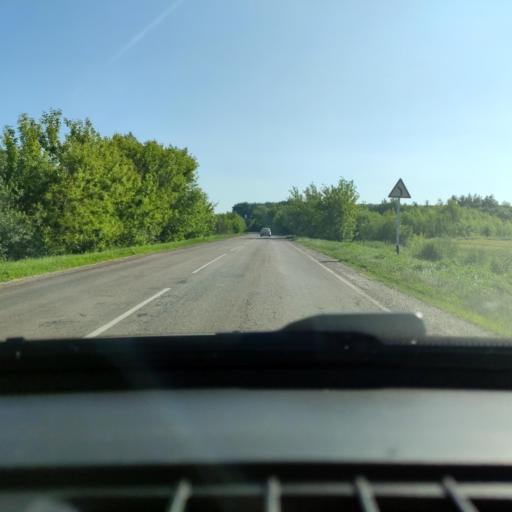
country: RU
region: Voronezj
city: Panino
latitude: 51.5996
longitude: 39.9795
